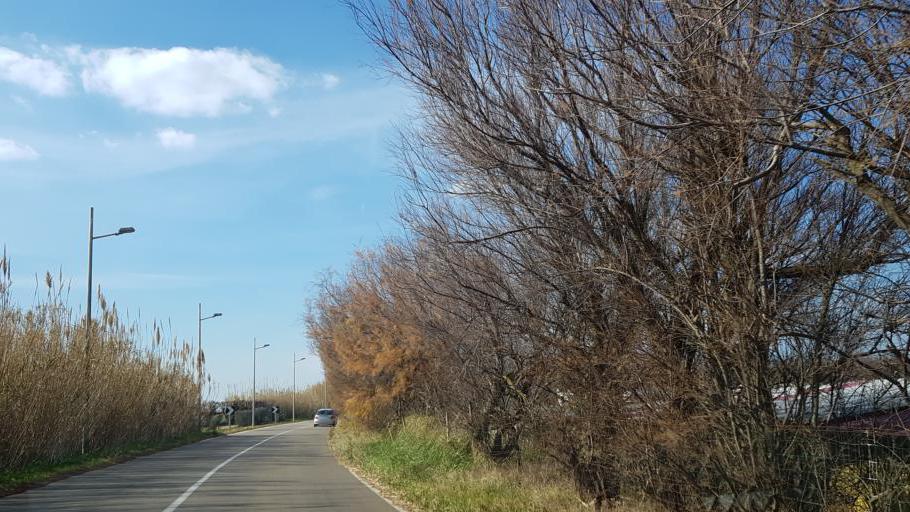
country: IT
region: Apulia
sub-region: Provincia di Brindisi
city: Brindisi
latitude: 40.6809
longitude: 17.8930
